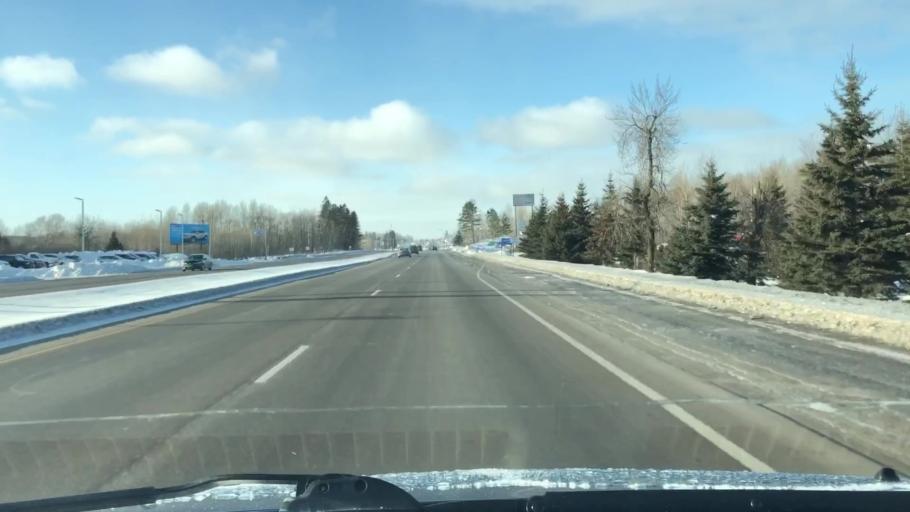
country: US
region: Minnesota
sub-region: Saint Louis County
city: Hermantown
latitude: 46.8162
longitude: -92.1768
